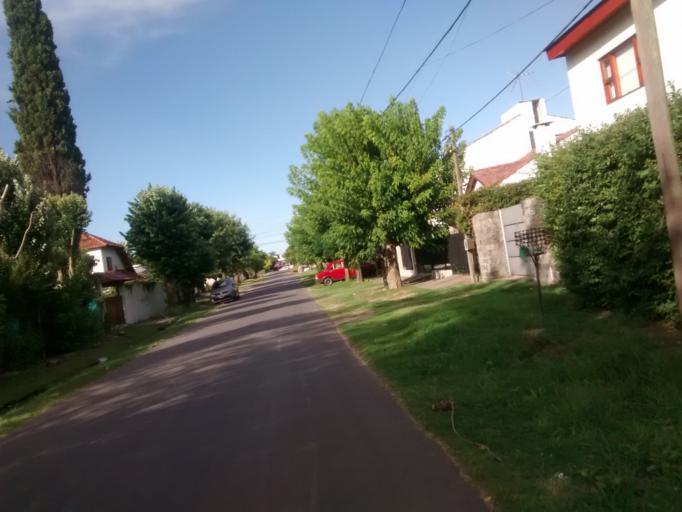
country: AR
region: Buenos Aires
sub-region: Partido de La Plata
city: La Plata
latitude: -34.8568
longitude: -58.0783
